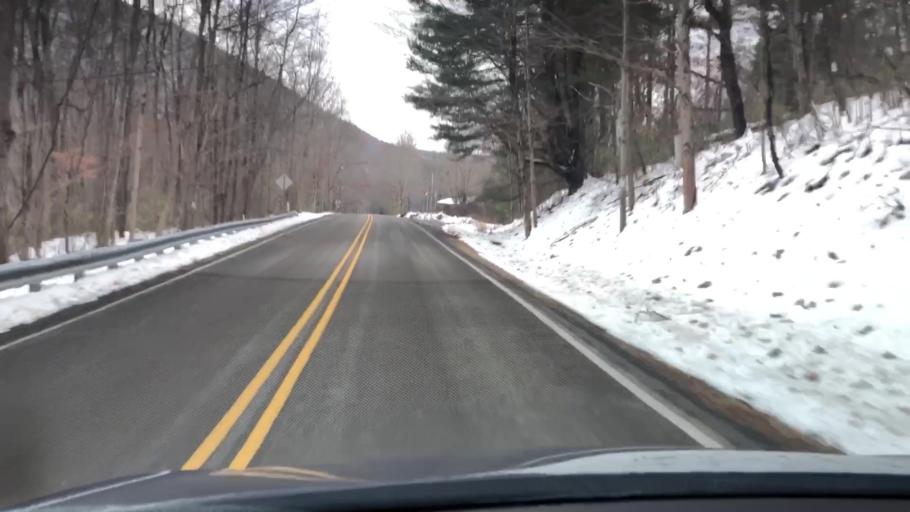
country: US
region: Pennsylvania
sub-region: Cameron County
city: Emporium
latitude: 41.3297
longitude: -78.3358
